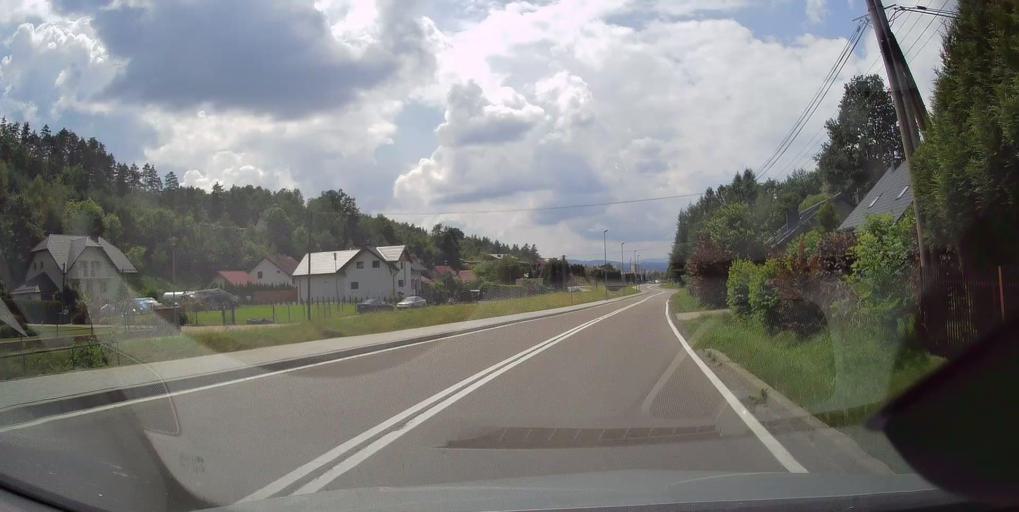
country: PL
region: Lesser Poland Voivodeship
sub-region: Powiat nowosadecki
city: Nowy Sacz
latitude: 49.6404
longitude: 20.7153
